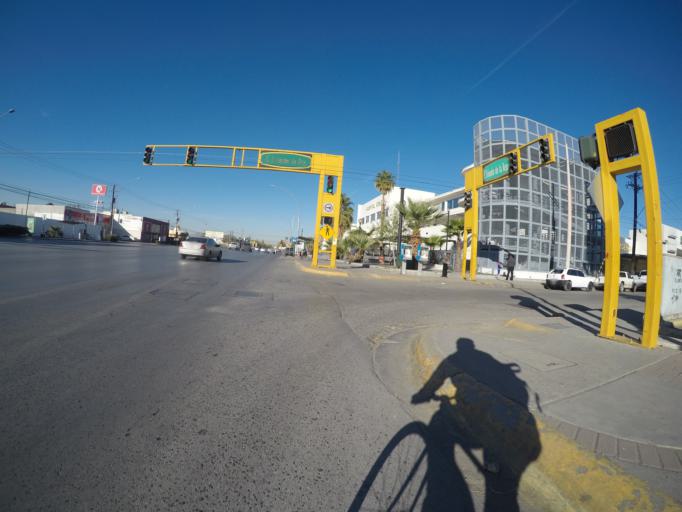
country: MX
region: Chihuahua
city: Ciudad Juarez
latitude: 31.7376
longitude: -106.4556
